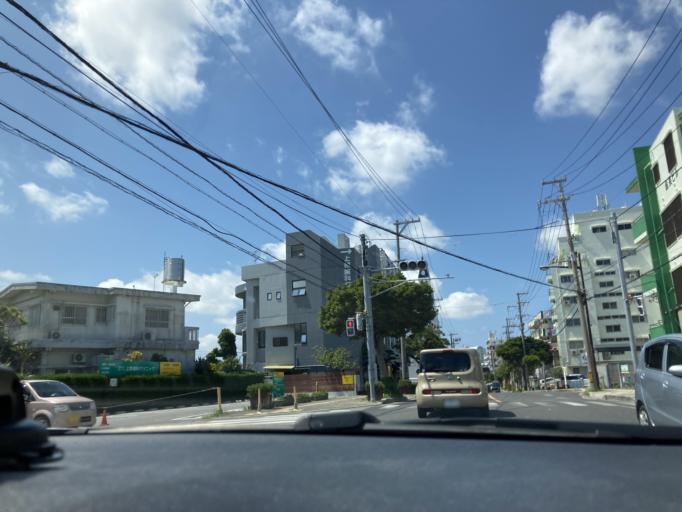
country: JP
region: Okinawa
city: Ginowan
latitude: 26.2380
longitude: 127.7388
